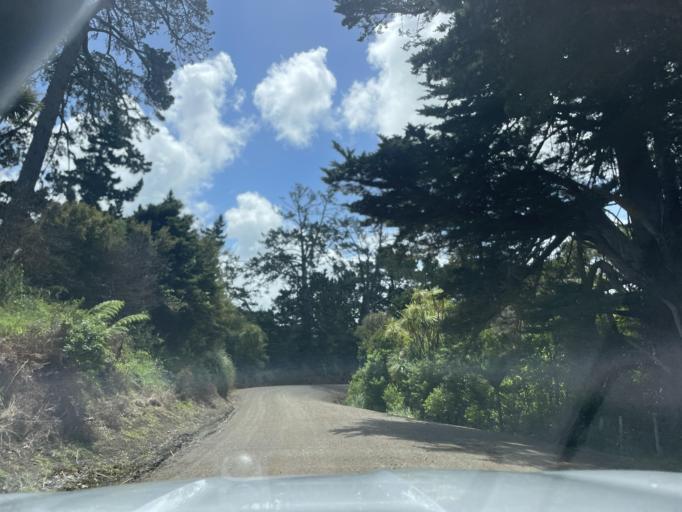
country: NZ
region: Auckland
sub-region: Auckland
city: Wellsford
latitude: -36.1844
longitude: 174.3209
